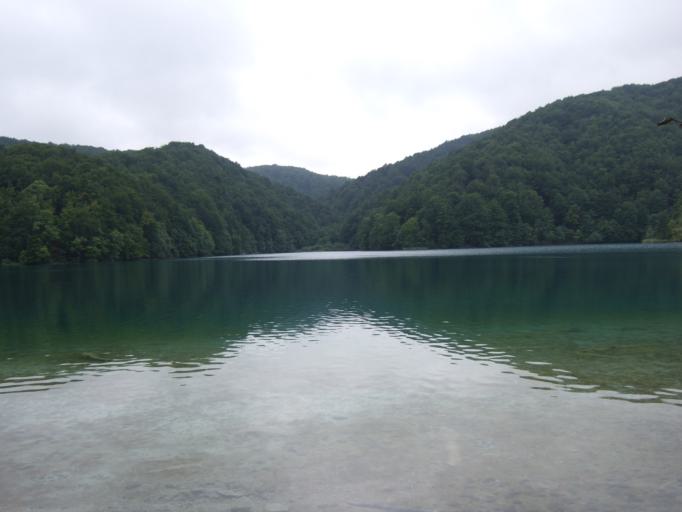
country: HR
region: Licko-Senjska
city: Jezerce
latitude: 44.8891
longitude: 15.6084
